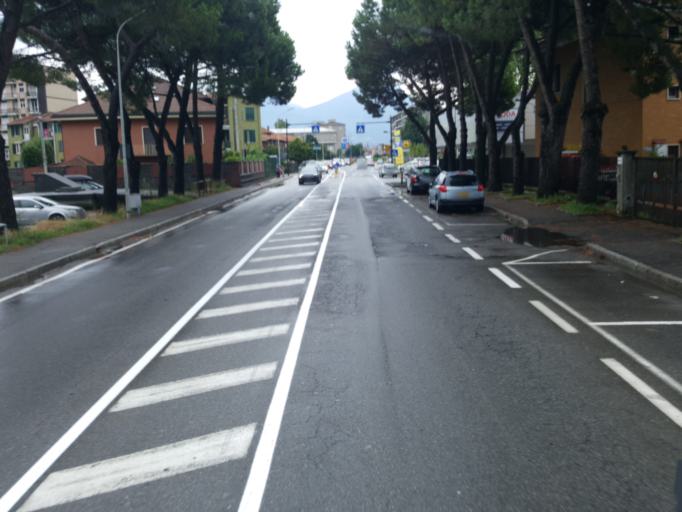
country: IT
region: Piedmont
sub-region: Provincia Verbano-Cusio-Ossola
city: Verbania
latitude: 45.9293
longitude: 8.5491
